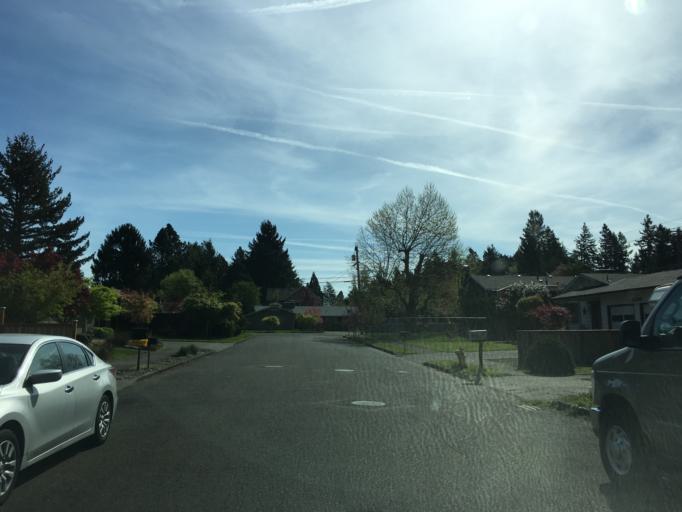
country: US
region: Oregon
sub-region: Multnomah County
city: Lents
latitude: 45.5341
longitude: -122.5166
